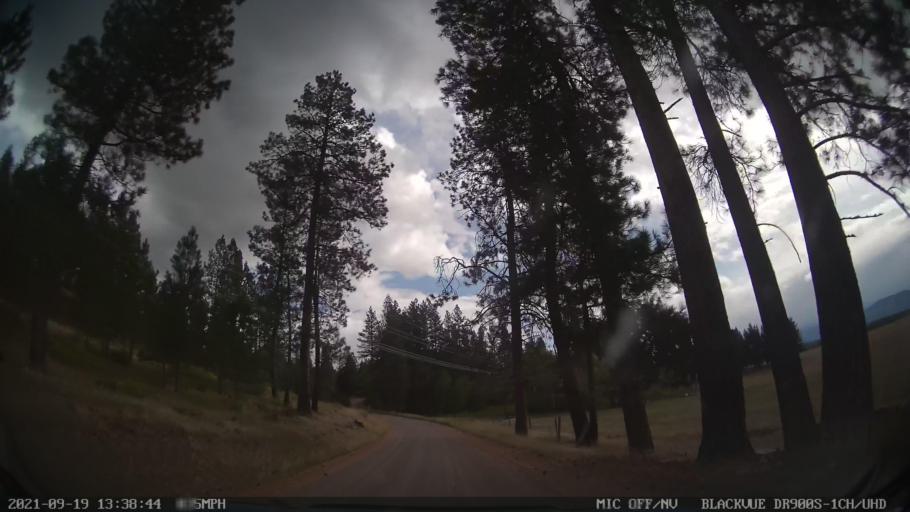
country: US
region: Montana
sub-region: Missoula County
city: Seeley Lake
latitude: 47.1027
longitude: -113.2691
